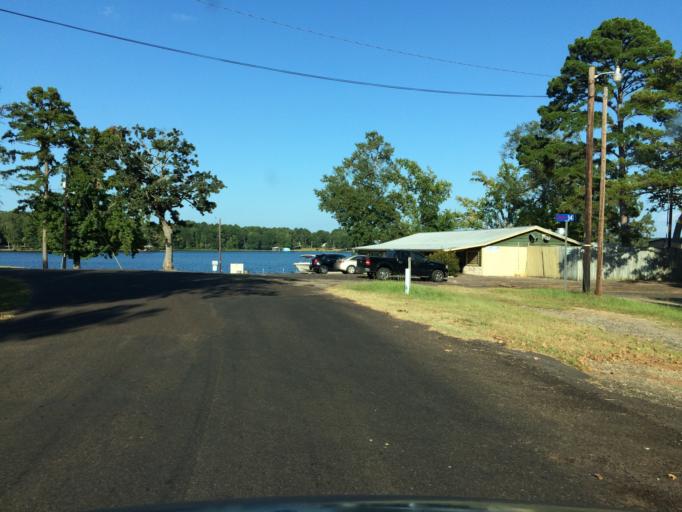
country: US
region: Texas
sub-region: Wood County
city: Hawkins
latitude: 32.6213
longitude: -95.2538
